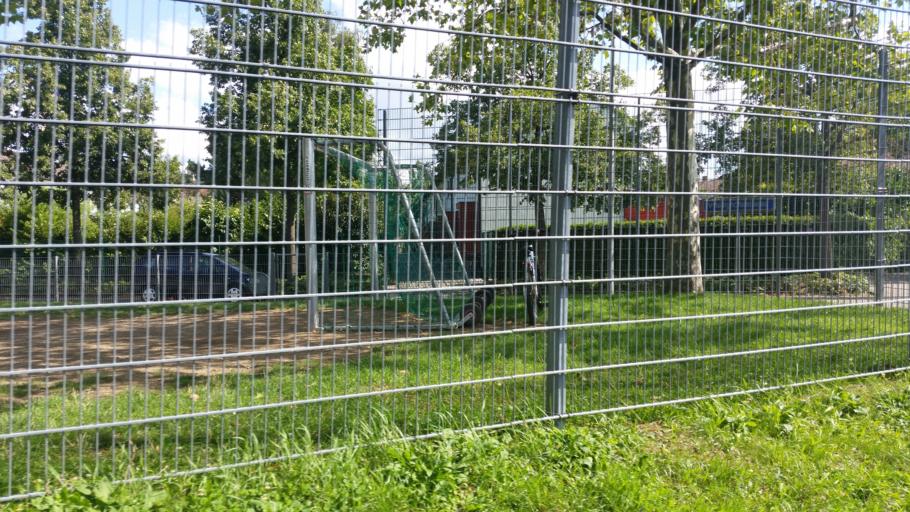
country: CH
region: Basel-City
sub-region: Basel-Stadt
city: Basel
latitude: 47.5675
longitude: 7.5595
